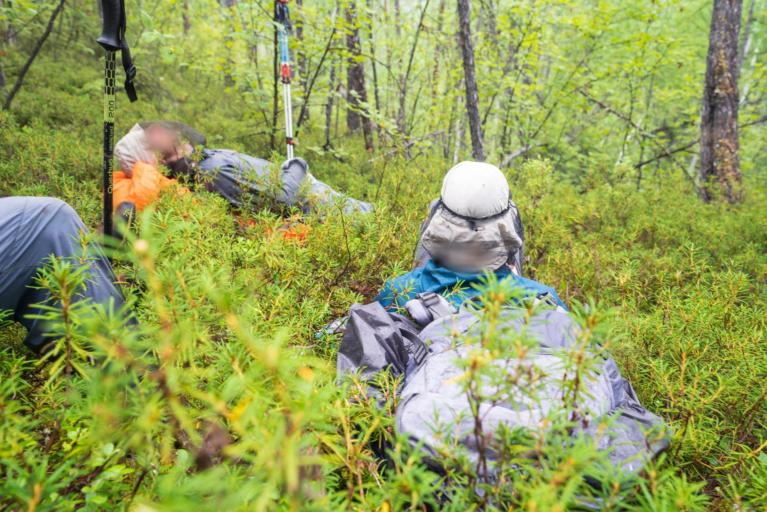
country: RU
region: Transbaikal Territory
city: Kuanda
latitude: 56.4593
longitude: 116.4025
